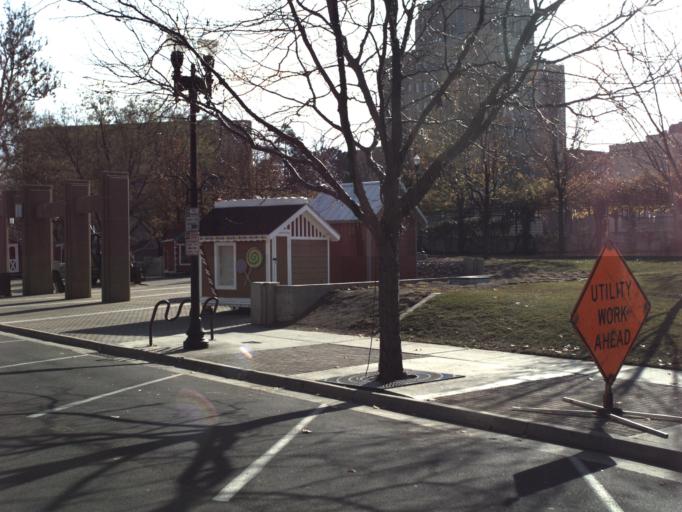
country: US
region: Utah
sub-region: Weber County
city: Ogden
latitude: 41.2207
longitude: -111.9725
